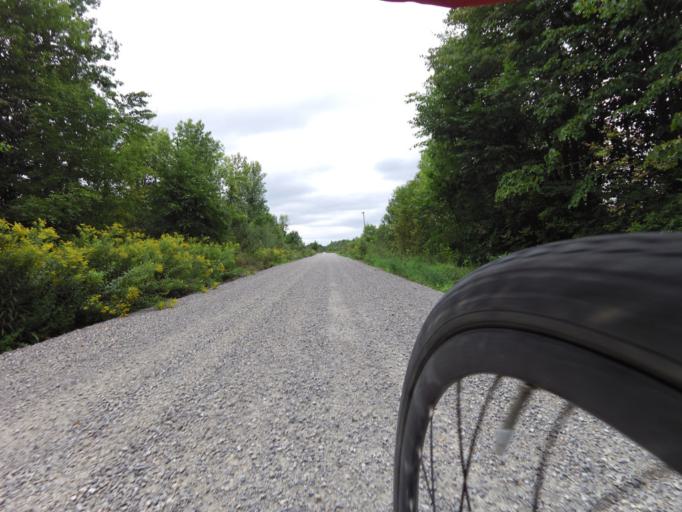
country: CA
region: Ontario
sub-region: Lanark County
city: Smiths Falls
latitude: 44.9526
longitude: -76.0453
